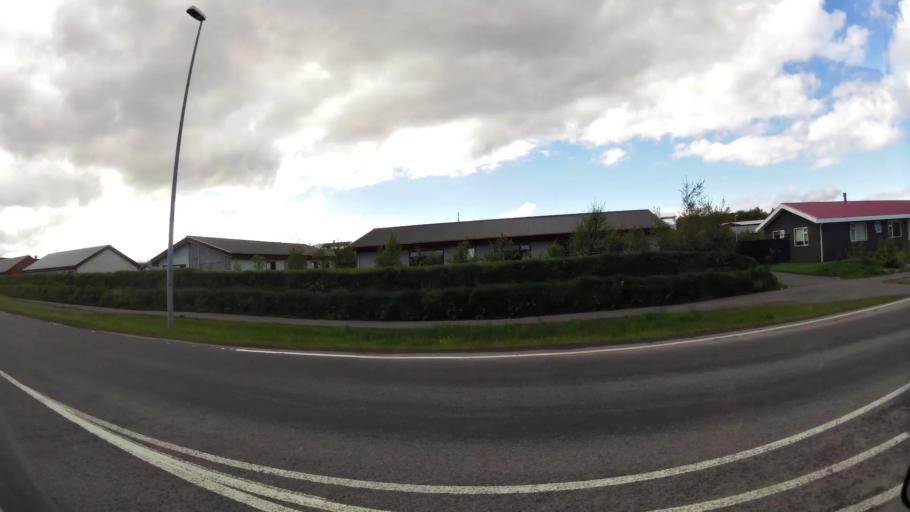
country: IS
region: East
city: Egilsstadir
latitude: 65.2600
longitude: -14.3891
